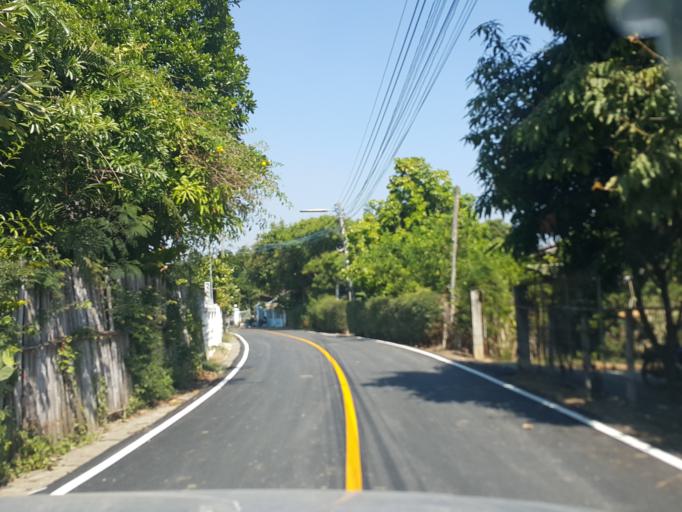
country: TH
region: Chiang Mai
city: San Kamphaeng
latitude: 18.8048
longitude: 99.1270
